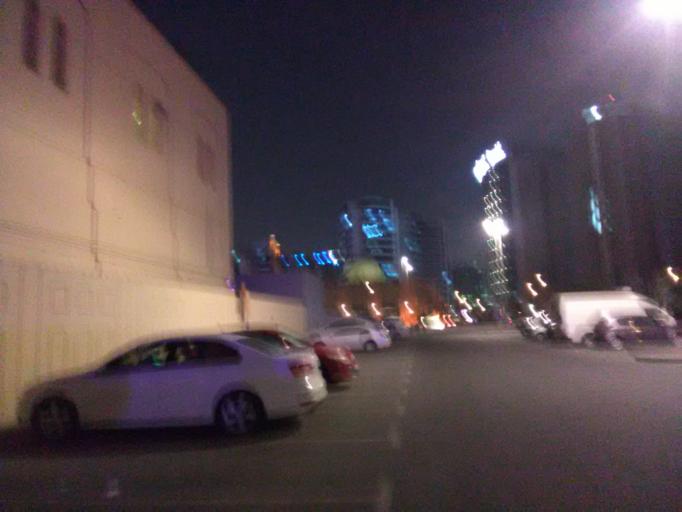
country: AE
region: Ash Shariqah
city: Sharjah
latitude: 25.2568
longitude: 55.3274
